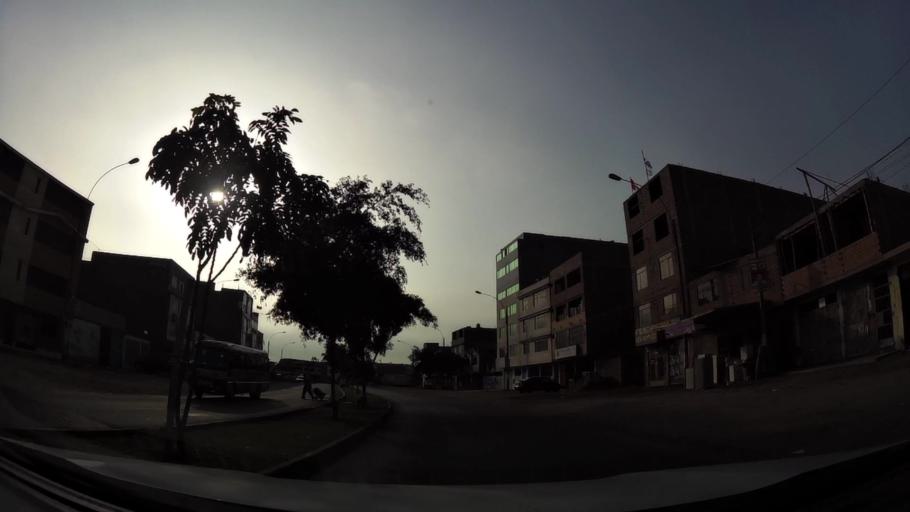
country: PE
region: Lima
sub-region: Lima
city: Independencia
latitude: -11.9960
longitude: -77.1040
